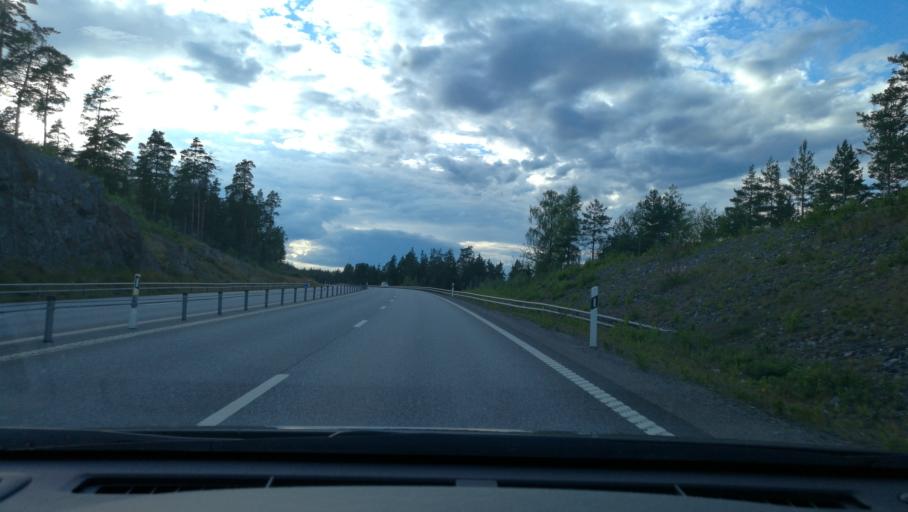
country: SE
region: OEstergoetland
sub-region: Norrkopings Kommun
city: Svartinge
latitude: 58.6591
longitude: 16.0389
